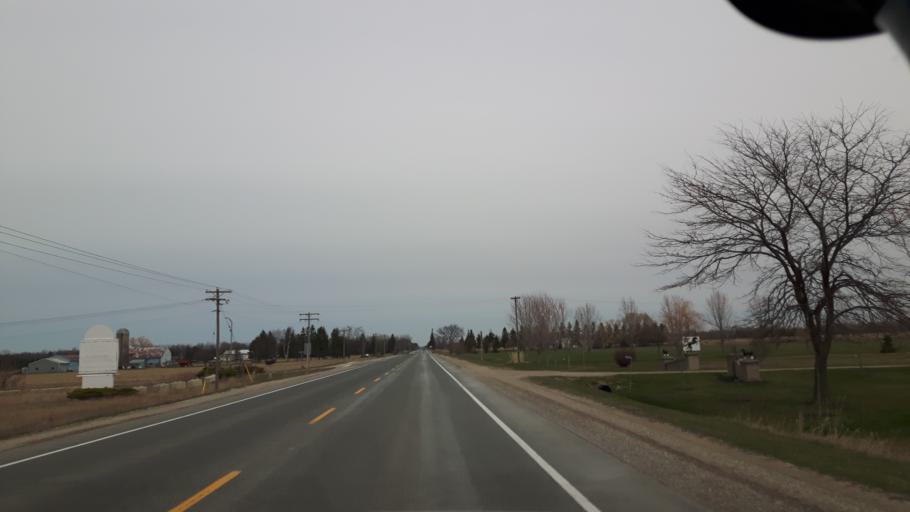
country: CA
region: Ontario
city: Goderich
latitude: 43.6900
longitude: -81.7056
